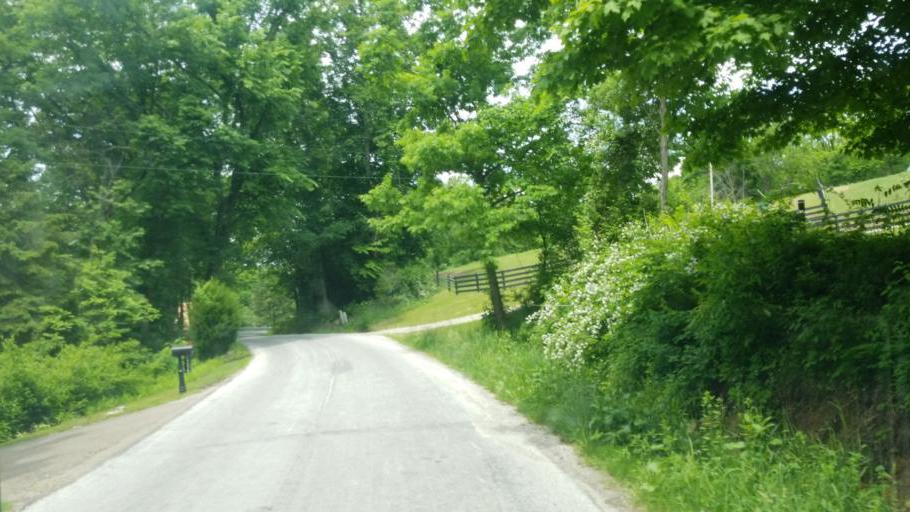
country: US
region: Ohio
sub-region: Coshocton County
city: West Lafayette
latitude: 40.3826
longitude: -81.7956
